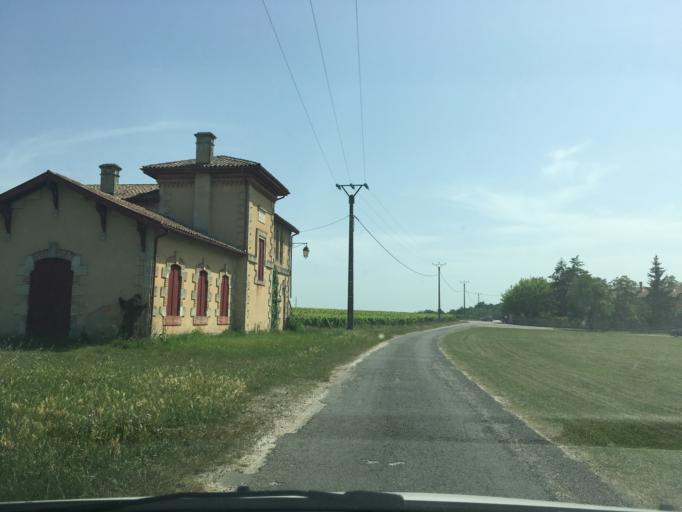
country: FR
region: Aquitaine
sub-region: Departement de la Gironde
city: Cantenac
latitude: 45.0123
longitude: -0.6431
